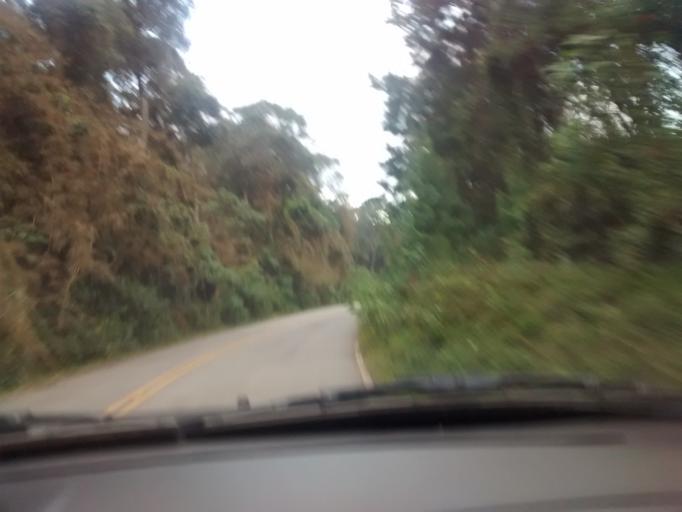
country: BR
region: Sao Paulo
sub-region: Campos Do Jordao
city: Campos do Jordao
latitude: -22.6506
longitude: -45.6360
